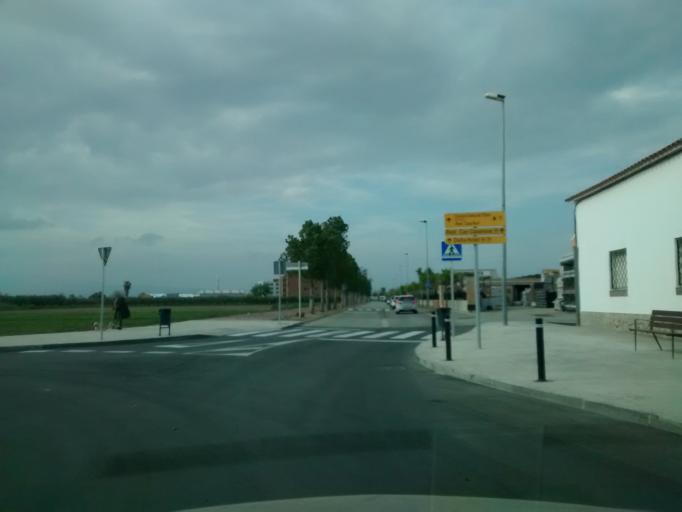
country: ES
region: Catalonia
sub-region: Provincia de Tarragona
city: Deltebre
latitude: 40.7187
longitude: 0.7210
